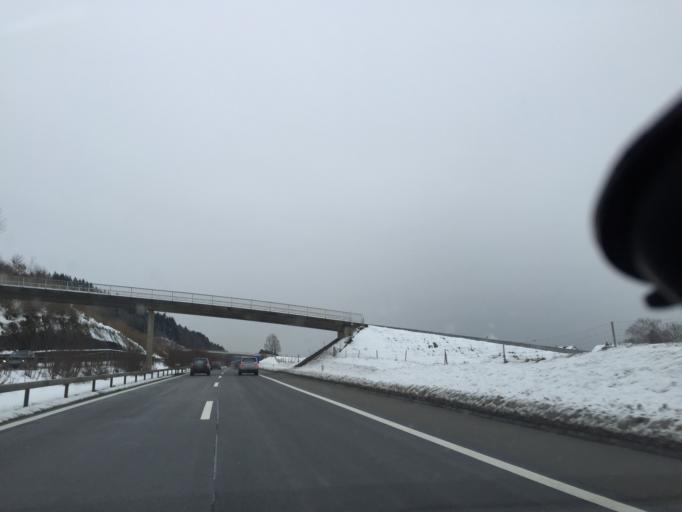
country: CH
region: Zurich
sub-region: Bezirk Horgen
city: Horgen / Allmend
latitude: 47.2348
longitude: 8.6172
